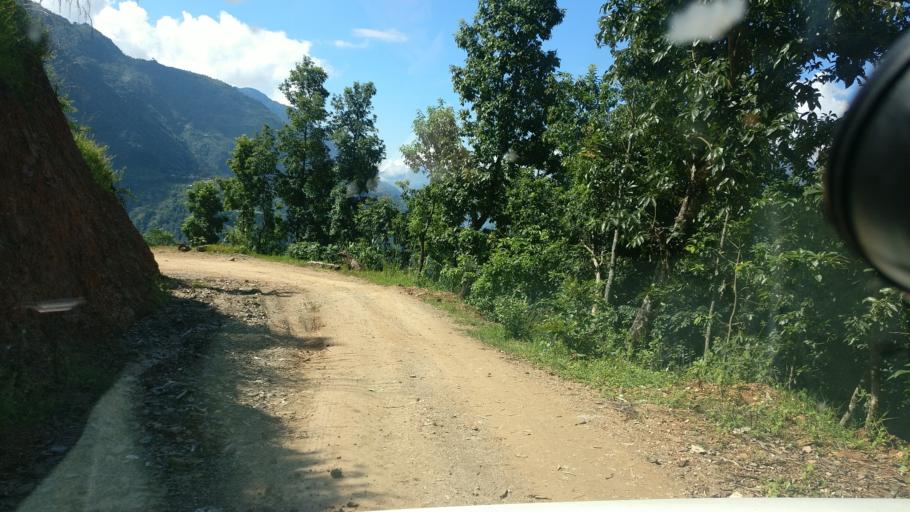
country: NP
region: Western Region
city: Baglung
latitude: 28.1379
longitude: 83.6480
